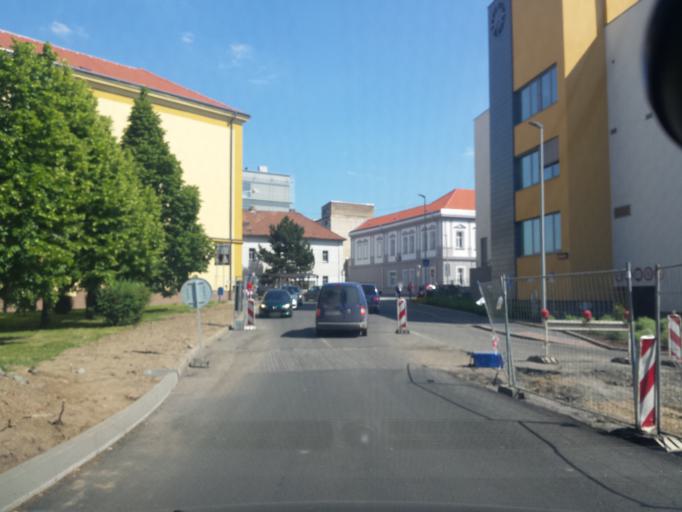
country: CZ
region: Central Bohemia
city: Kralupy nad Vltavou
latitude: 50.2417
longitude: 14.3108
